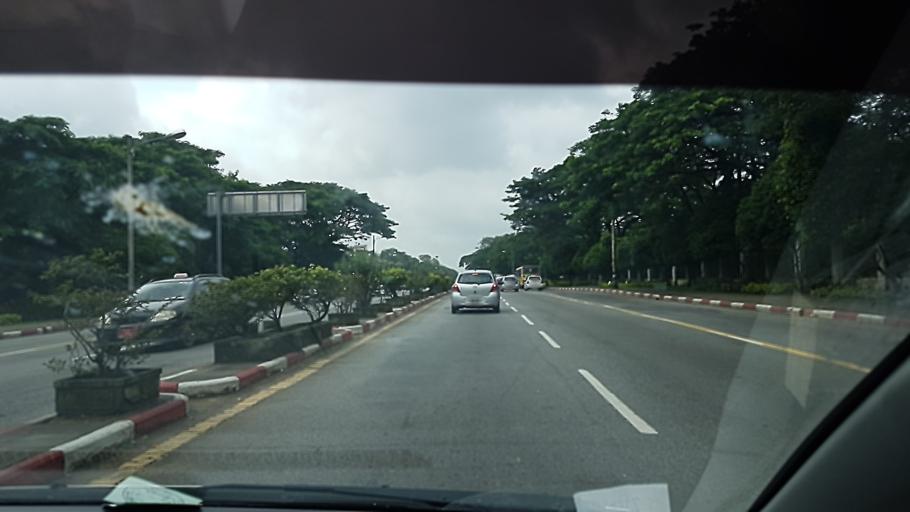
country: MM
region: Yangon
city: Yangon
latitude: 16.7976
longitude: 96.1389
